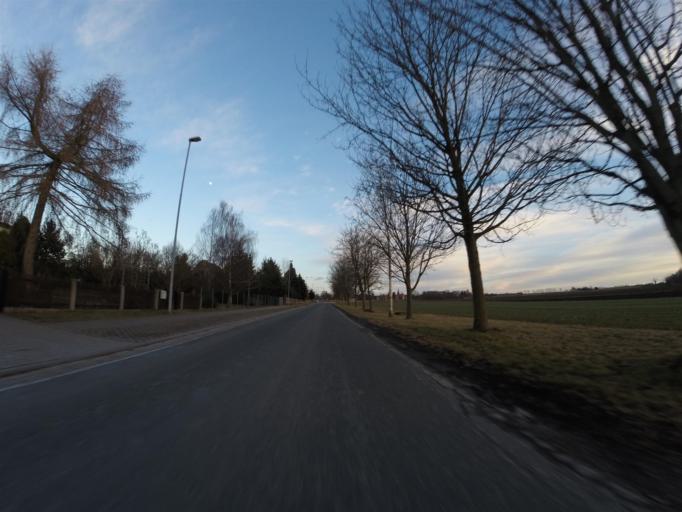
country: DE
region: Thuringia
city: Lehesten
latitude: 51.0095
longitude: 11.5557
